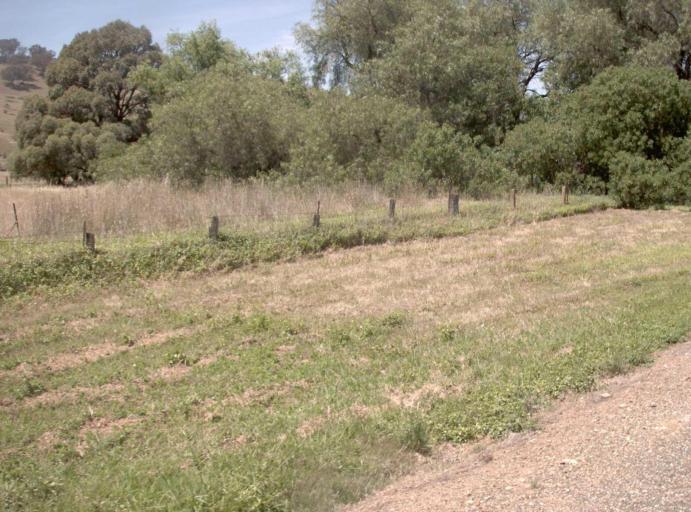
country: AU
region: Victoria
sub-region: East Gippsland
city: Bairnsdale
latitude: -37.2010
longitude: 147.7221
